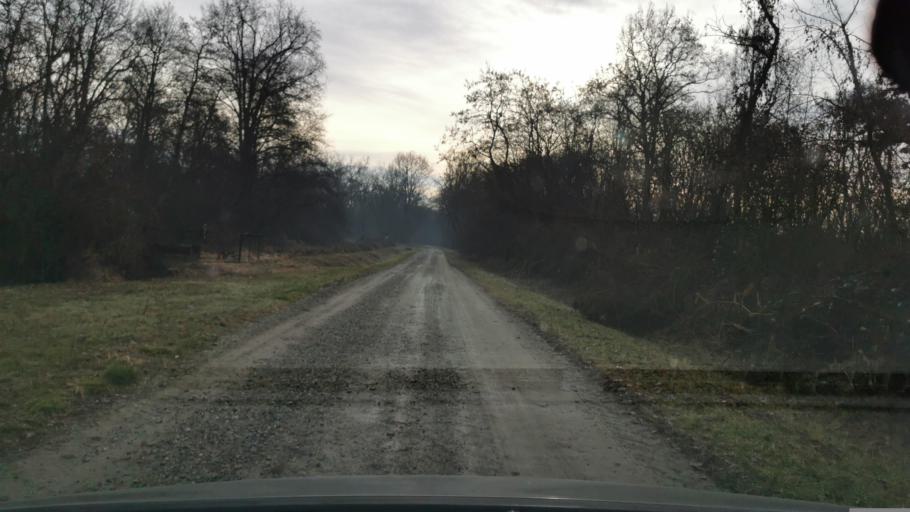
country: IT
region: Piedmont
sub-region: Provincia di Torino
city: Bosconero
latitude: 45.2690
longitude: 7.7813
